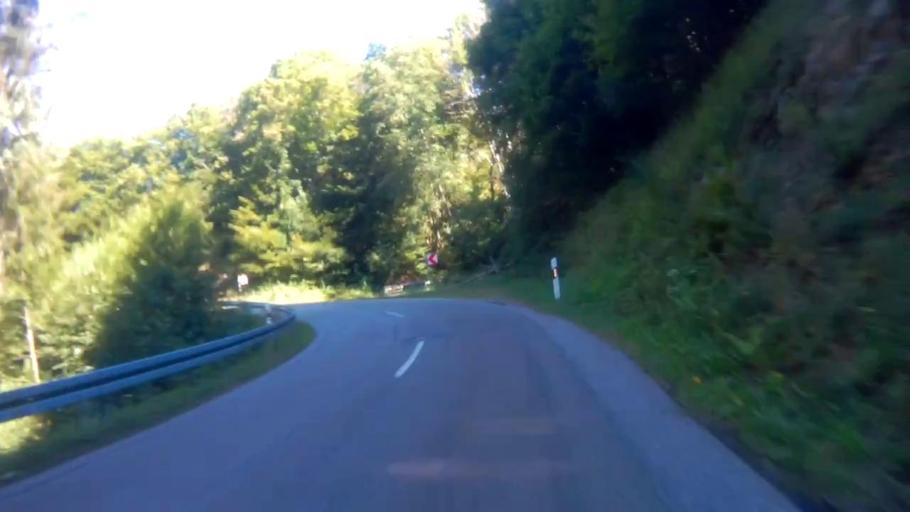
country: DE
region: Baden-Wuerttemberg
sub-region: Freiburg Region
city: Bollen
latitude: 47.7568
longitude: 7.7589
